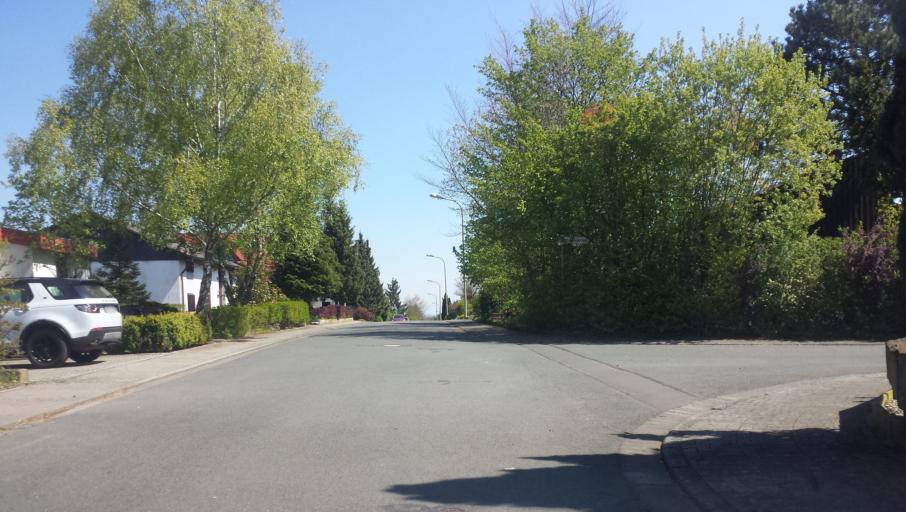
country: DE
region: Rheinland-Pfalz
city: Winnweiler
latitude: 49.5675
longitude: 7.8359
